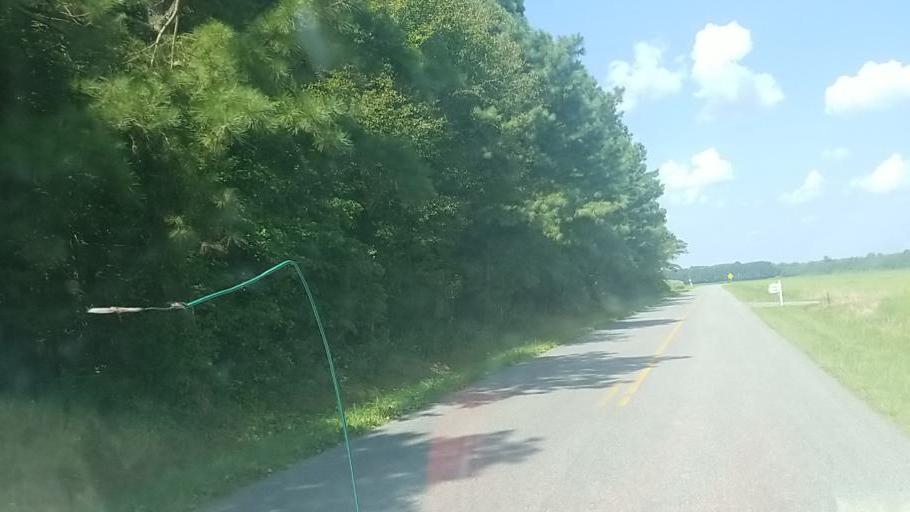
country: US
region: Maryland
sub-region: Worcester County
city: Berlin
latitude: 38.2974
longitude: -75.2680
